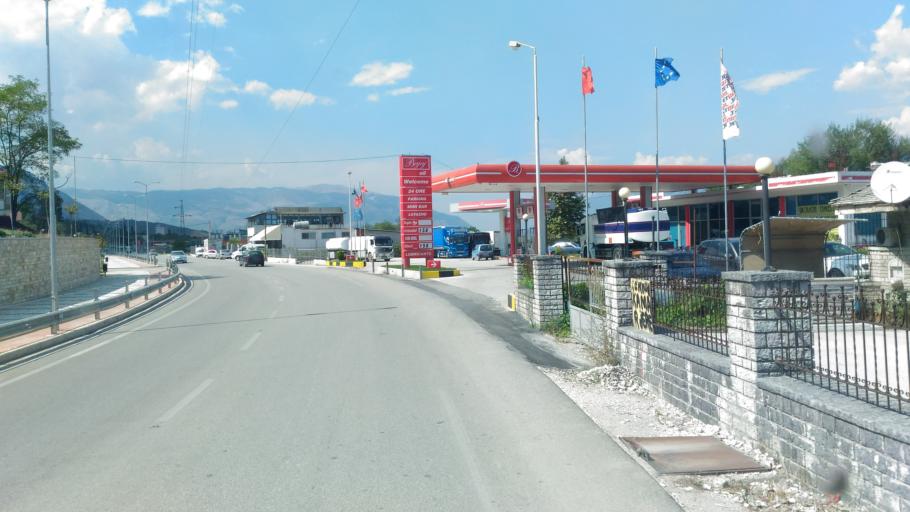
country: AL
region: Gjirokaster
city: Gjirokaster
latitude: 40.0861
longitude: 20.1431
